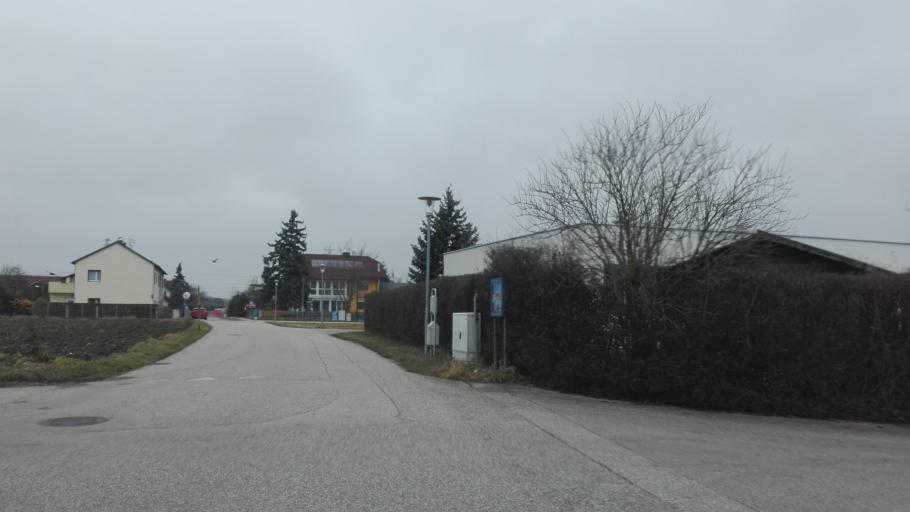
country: AT
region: Upper Austria
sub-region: Wels-Land
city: Marchtrenk
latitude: 48.2005
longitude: 14.1435
